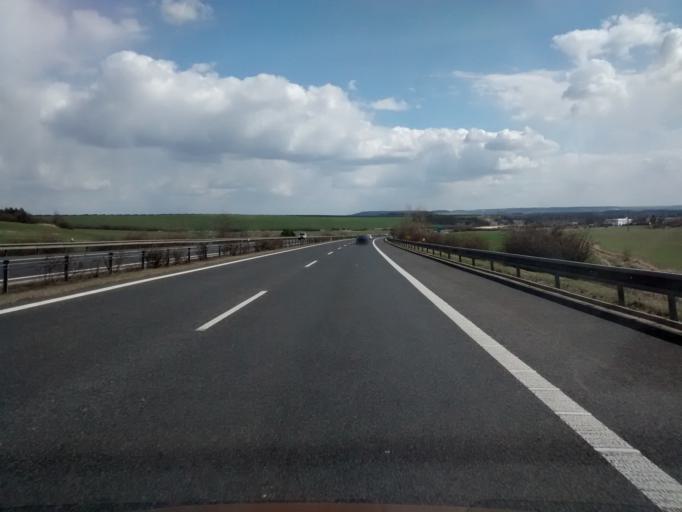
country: CZ
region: Central Bohemia
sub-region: Okres Melnik
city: Veltrusy
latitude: 50.3242
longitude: 14.3020
